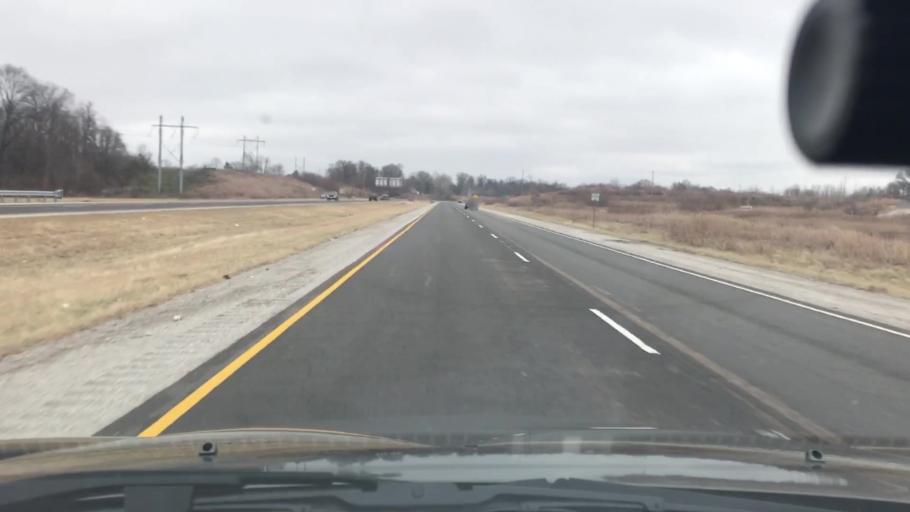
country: US
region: Illinois
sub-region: Madison County
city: Roxana
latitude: 38.8699
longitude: -90.0591
